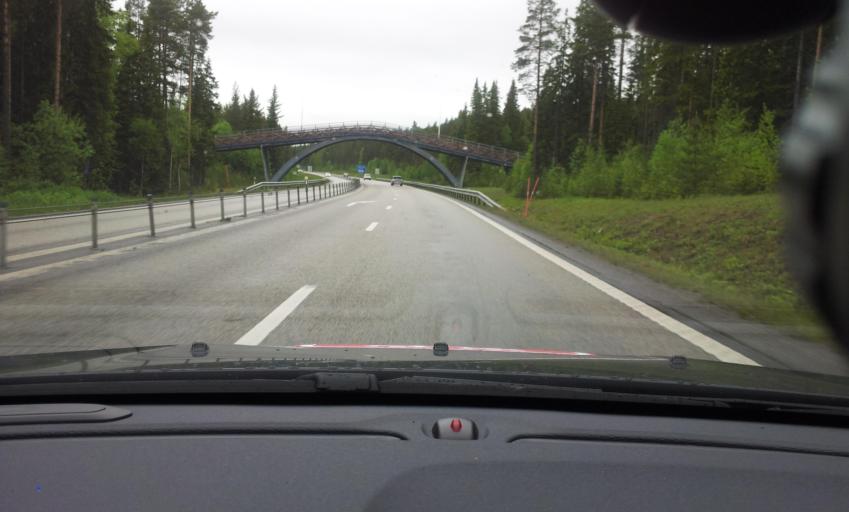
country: SE
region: Jaemtland
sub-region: OEstersunds Kommun
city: Ostersund
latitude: 63.1922
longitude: 14.6902
